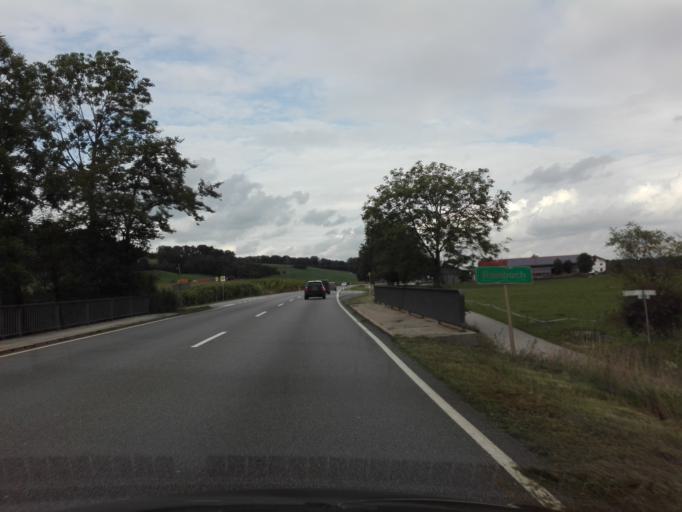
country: DE
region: Bavaria
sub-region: Upper Bavaria
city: Kirchdorf
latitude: 48.1686
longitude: 12.2120
